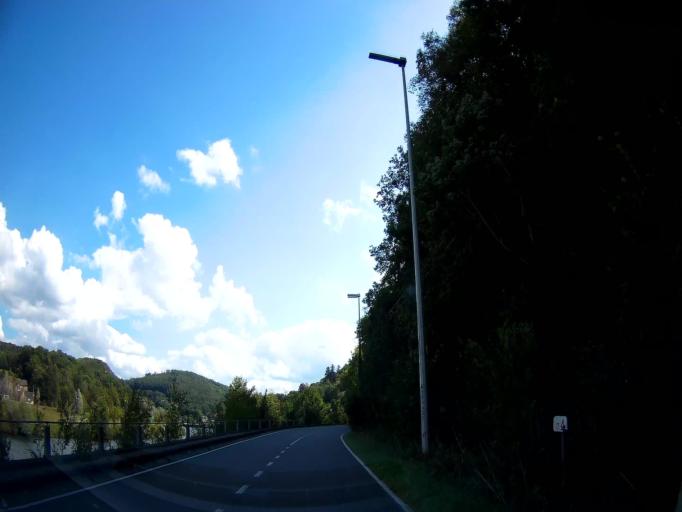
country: BE
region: Wallonia
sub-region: Province de Namur
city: Yvoir
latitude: 50.3407
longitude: 4.8595
